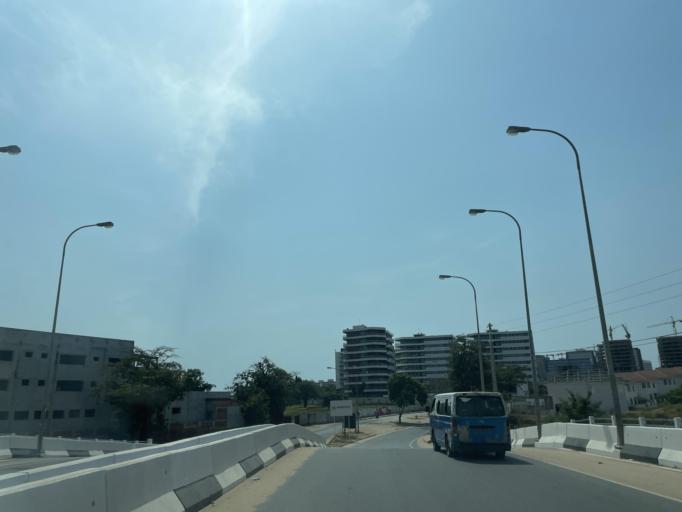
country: AO
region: Luanda
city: Luanda
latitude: -8.9267
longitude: 13.1974
